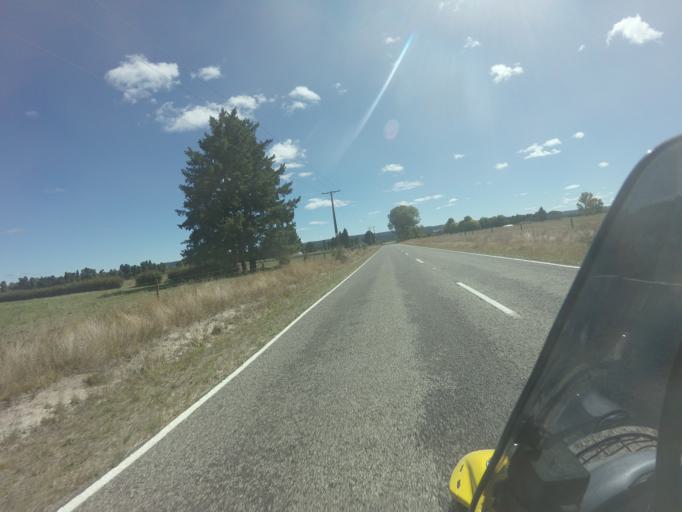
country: NZ
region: Bay of Plenty
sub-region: Whakatane District
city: Murupara
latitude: -38.4399
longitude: 176.7225
